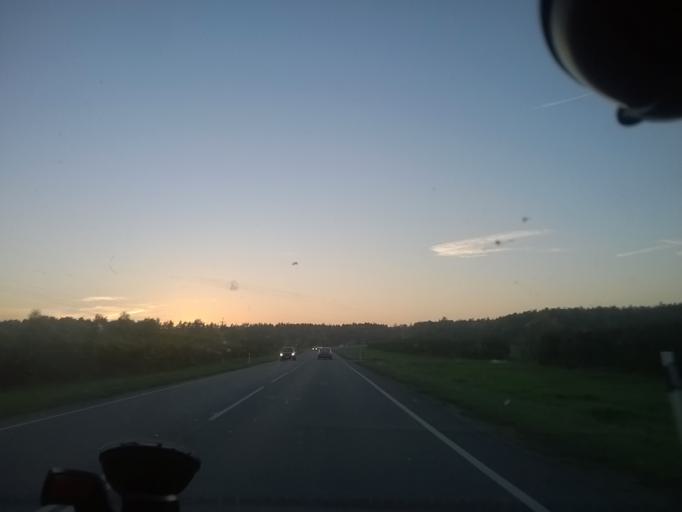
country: EE
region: Laeaene
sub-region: Ridala Parish
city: Uuemoisa
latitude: 58.9567
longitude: 23.7344
